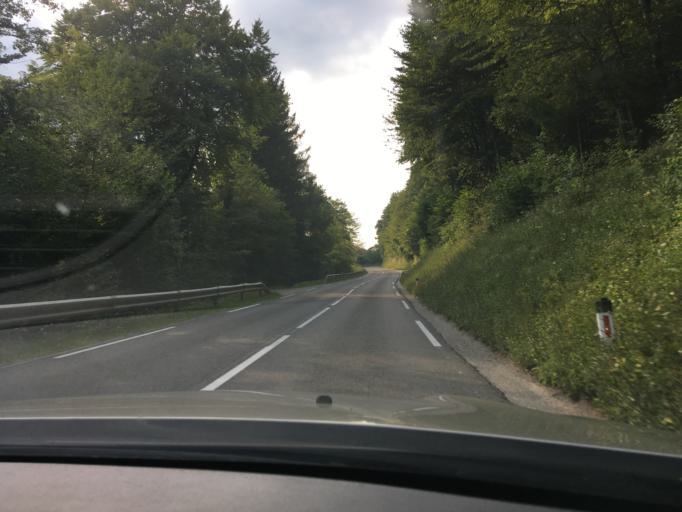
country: SI
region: Dolenjske Toplice
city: Dolenjske Toplice
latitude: 45.7820
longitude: 15.0032
